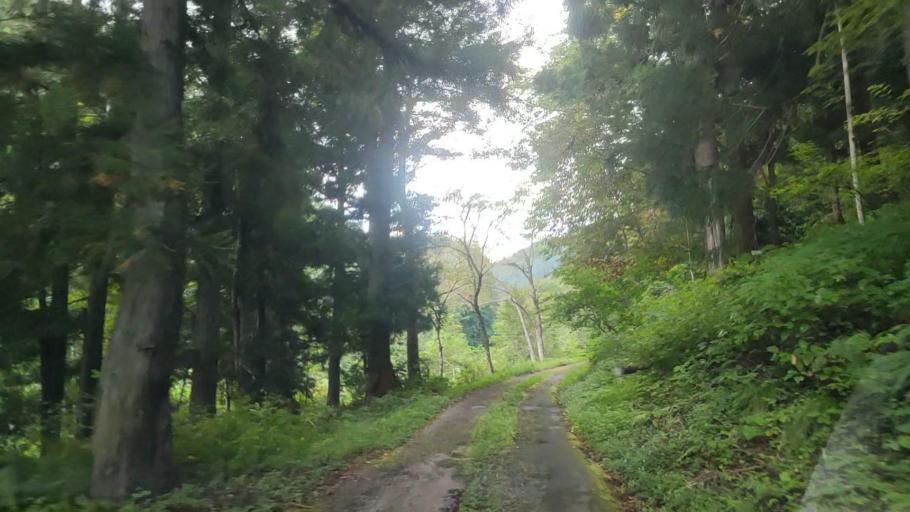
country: JP
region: Gifu
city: Takayama
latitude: 36.3206
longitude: 137.0831
